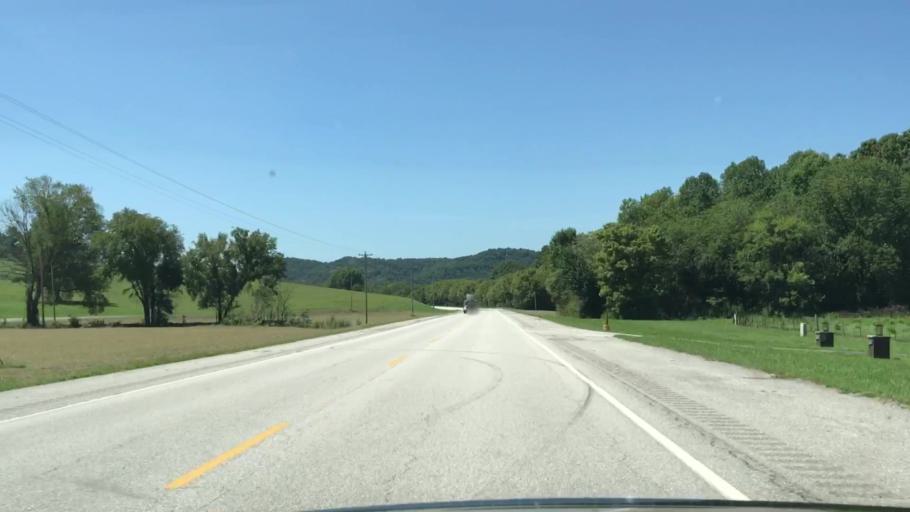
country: US
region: Tennessee
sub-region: Jackson County
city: Gainesboro
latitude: 36.4362
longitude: -85.6236
